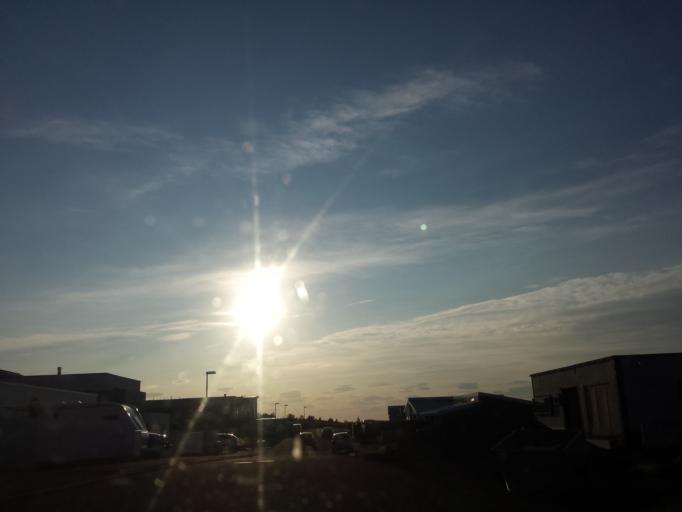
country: IS
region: Capital Region
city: Kopavogur
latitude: 64.0918
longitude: -21.8697
